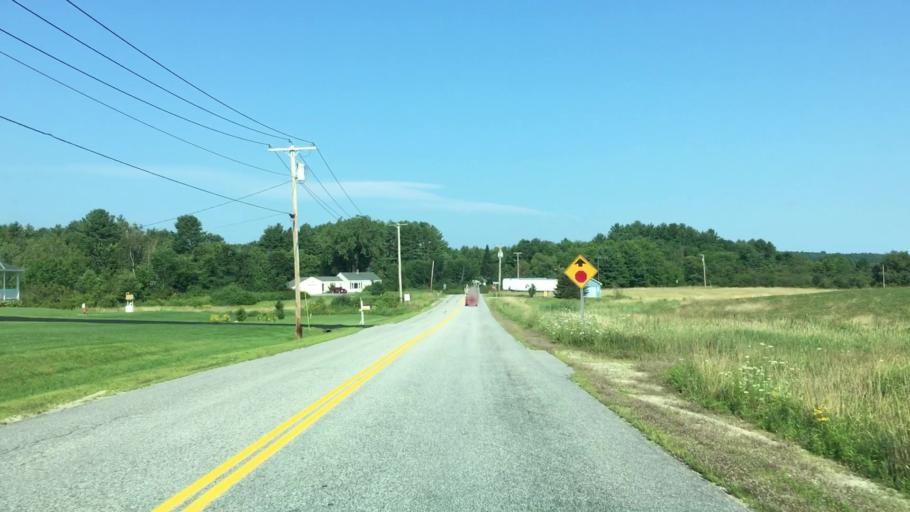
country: US
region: Maine
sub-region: Androscoggin County
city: Minot
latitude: 44.0443
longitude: -70.3270
